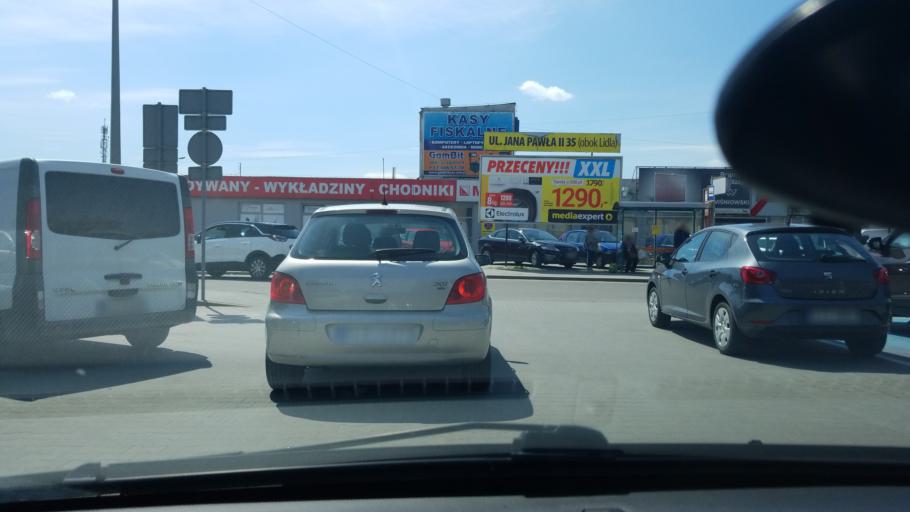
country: PL
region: Subcarpathian Voivodeship
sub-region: Powiat jasielski
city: Jaslo
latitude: 49.7457
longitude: 21.4821
